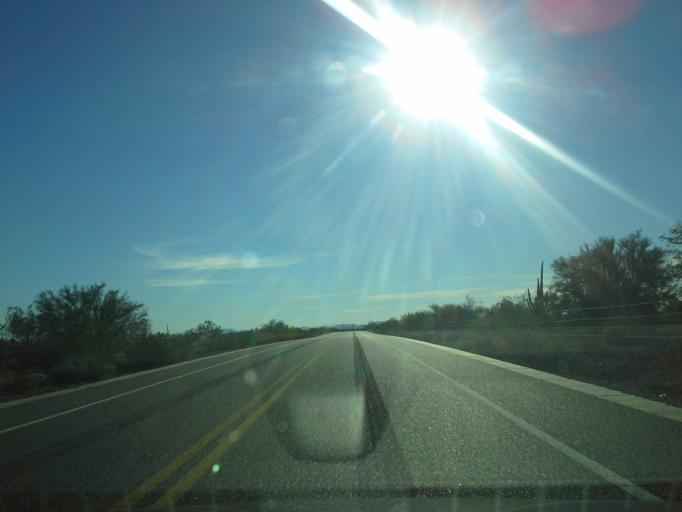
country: US
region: Arizona
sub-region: Pinal County
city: Gold Camp
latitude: 33.3011
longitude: -111.3779
